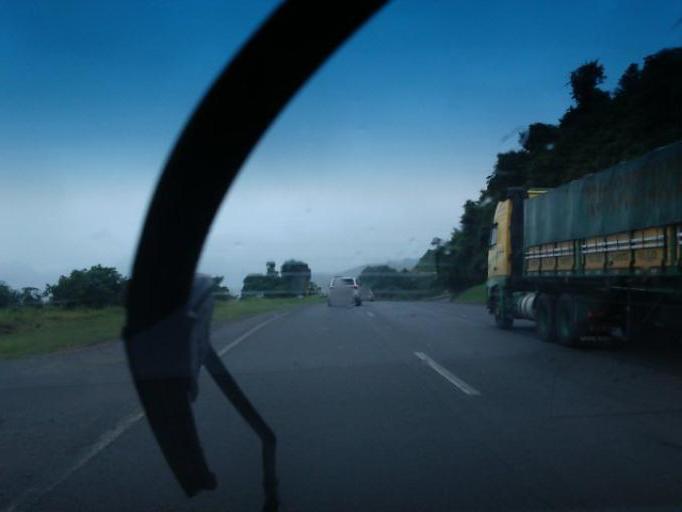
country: BR
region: Sao Paulo
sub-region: Cajati
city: Cajati
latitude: -24.9677
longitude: -48.4815
